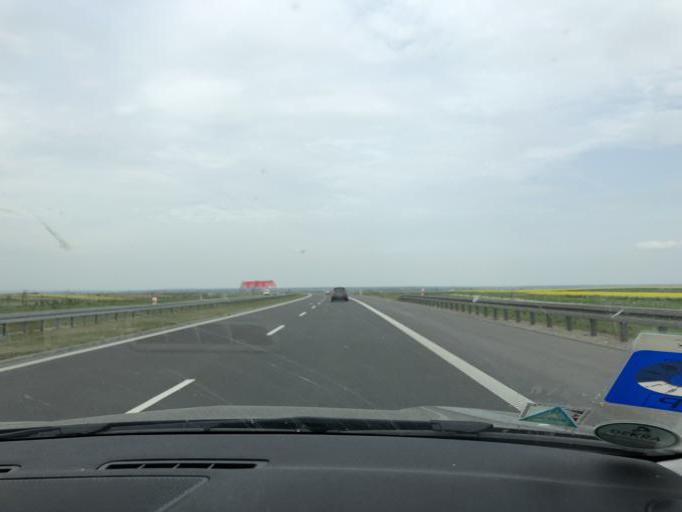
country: PL
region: Subcarpathian Voivodeship
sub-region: Powiat przeworski
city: Mirocin
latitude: 50.0562
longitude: 22.5698
